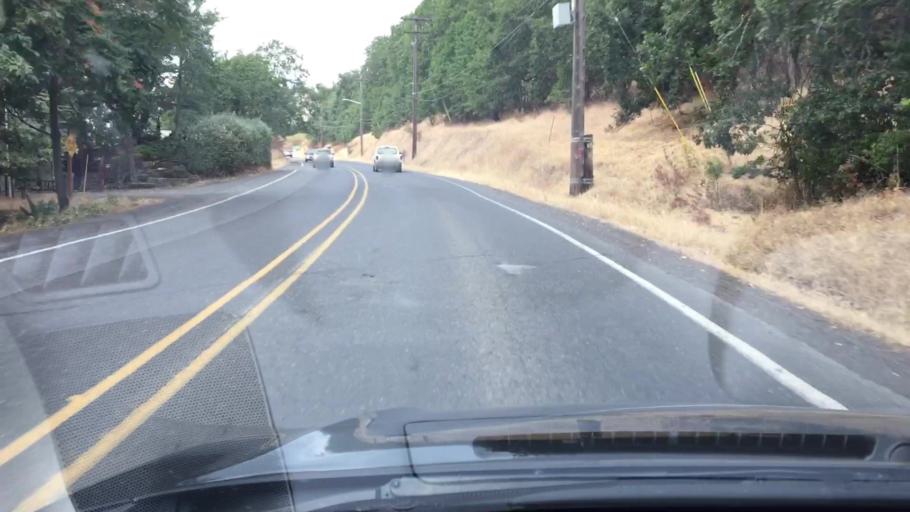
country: US
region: Washington
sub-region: Klickitat County
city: White Salmon
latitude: 45.7195
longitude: -121.4672
